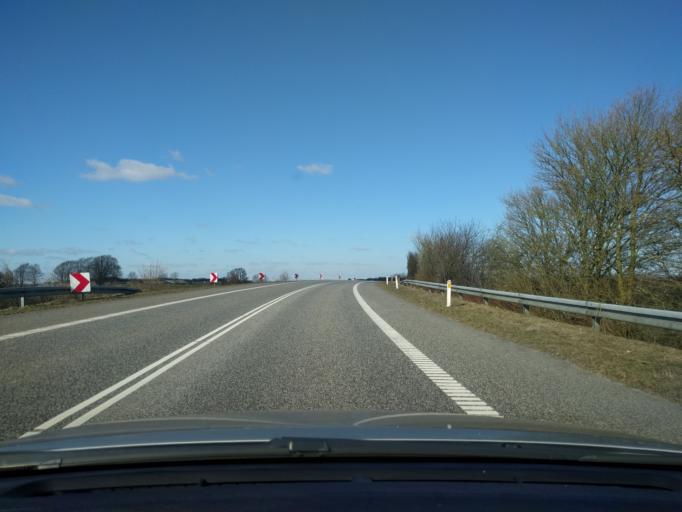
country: DK
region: South Denmark
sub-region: Aabenraa Kommune
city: Lojt Kirkeby
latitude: 55.1430
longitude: 9.4345
